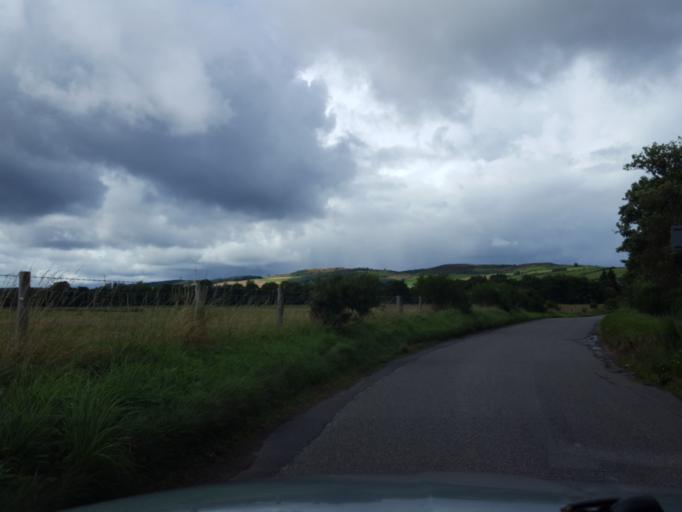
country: GB
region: Scotland
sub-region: Aberdeenshire
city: Torphins
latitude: 57.0181
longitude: -2.5896
